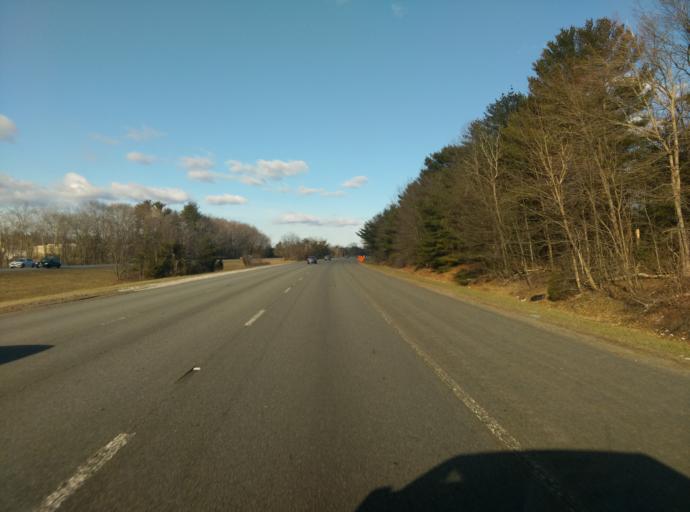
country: US
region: Massachusetts
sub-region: Essex County
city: Amesbury
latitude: 42.8357
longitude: -70.9582
